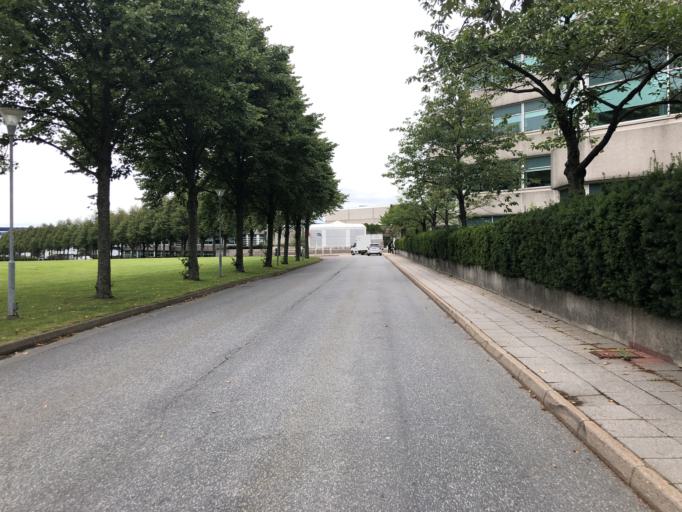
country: SE
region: Vaestra Goetaland
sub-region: Goteborg
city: Majorna
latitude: 57.7282
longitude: 11.8657
